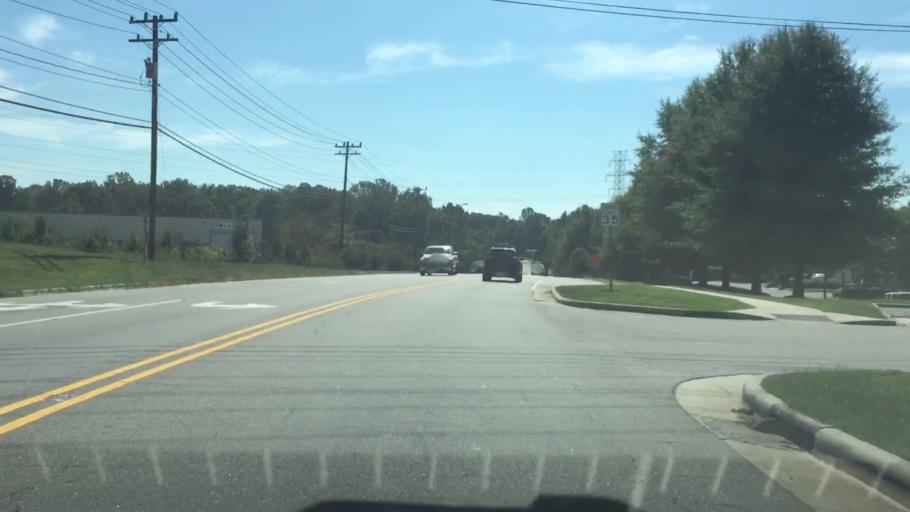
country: US
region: North Carolina
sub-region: Iredell County
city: Mooresville
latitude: 35.5948
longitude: -80.8162
